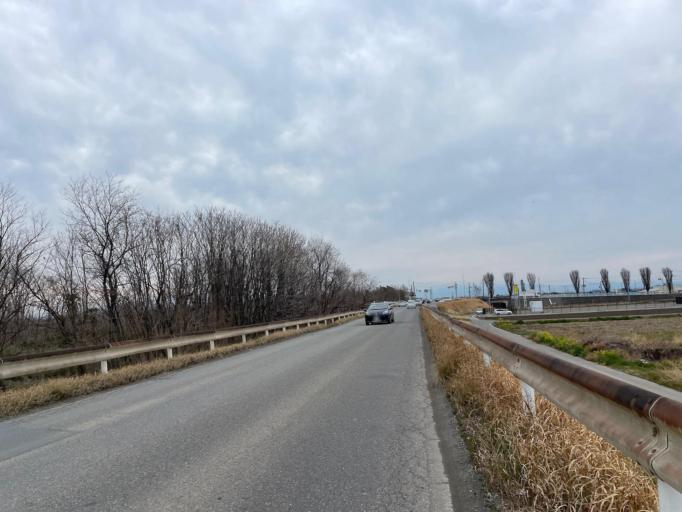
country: JP
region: Gunma
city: Fujioka
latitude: 36.2340
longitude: 139.0988
